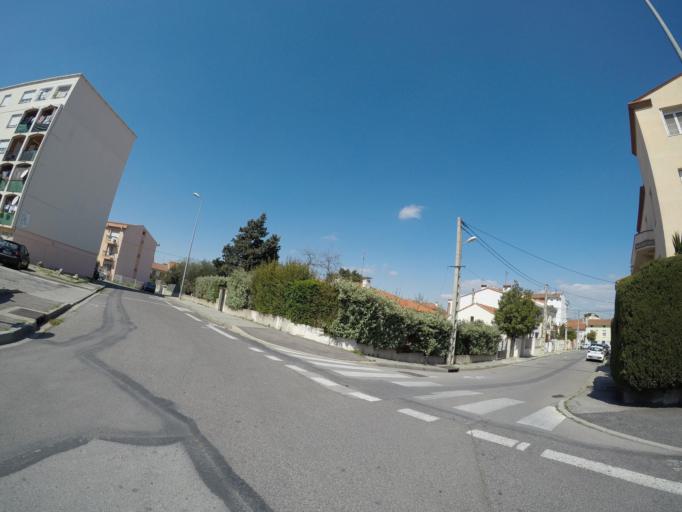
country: FR
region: Languedoc-Roussillon
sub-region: Departement des Pyrenees-Orientales
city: Perpignan
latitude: 42.6944
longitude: 2.9104
